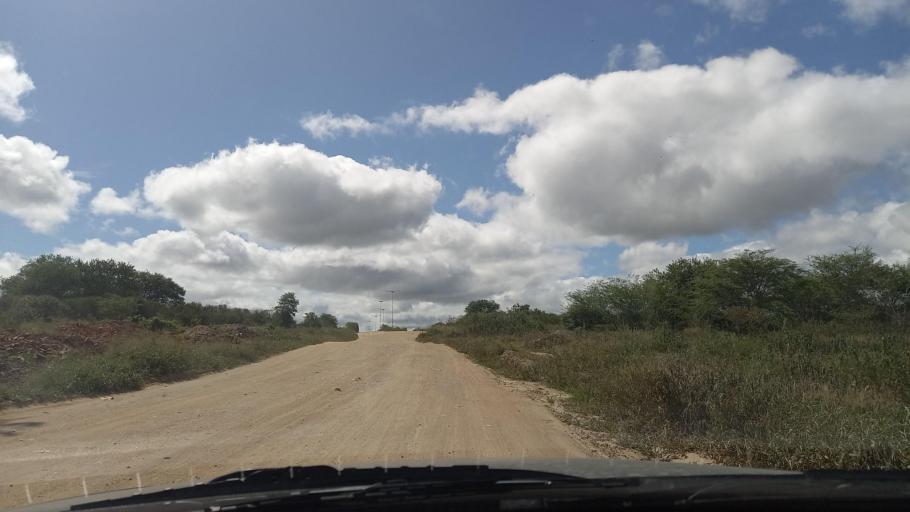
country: BR
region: Pernambuco
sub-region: Caruaru
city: Caruaru
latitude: -8.2239
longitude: -35.9881
